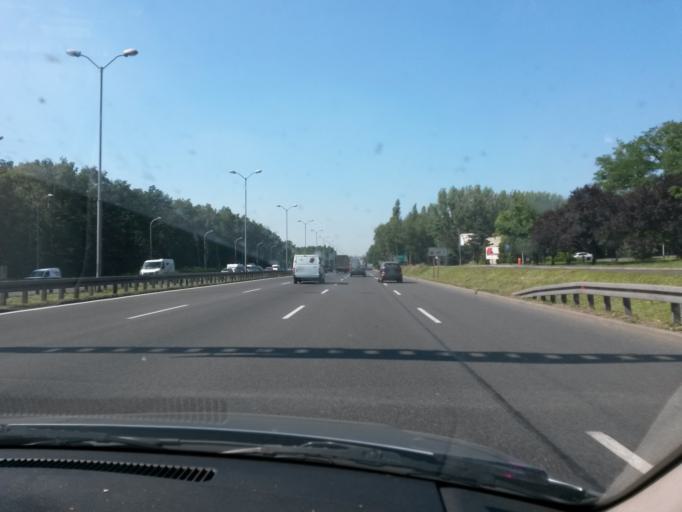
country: PL
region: Silesian Voivodeship
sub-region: Katowice
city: Katowice
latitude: 50.2459
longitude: 19.0507
